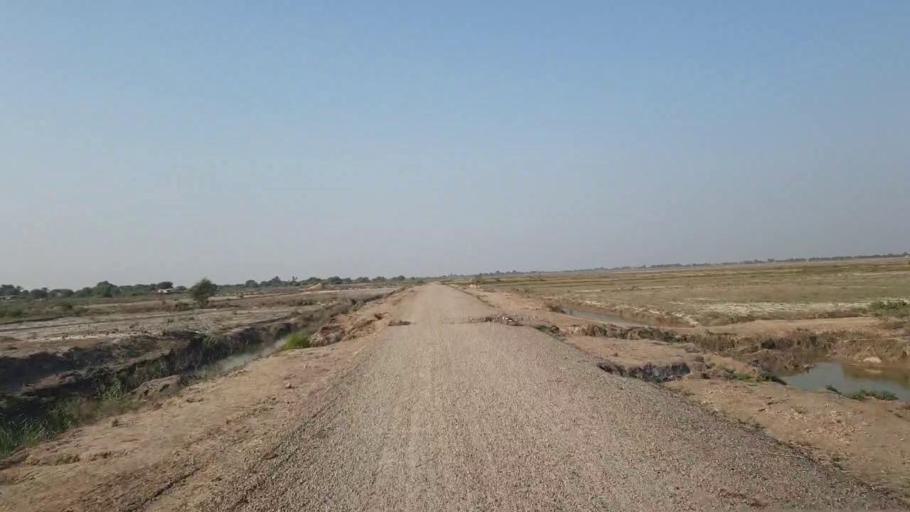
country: PK
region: Sindh
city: Kario
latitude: 24.9047
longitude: 68.6202
